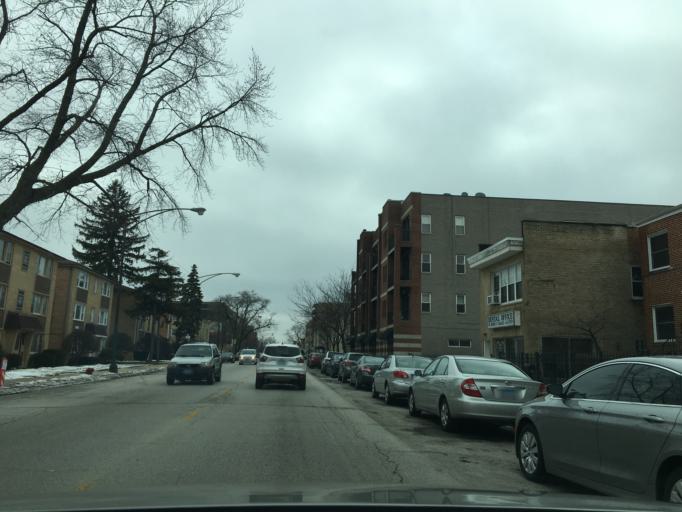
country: US
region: Illinois
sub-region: Cook County
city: Elmwood Park
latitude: 41.9357
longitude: -87.8067
